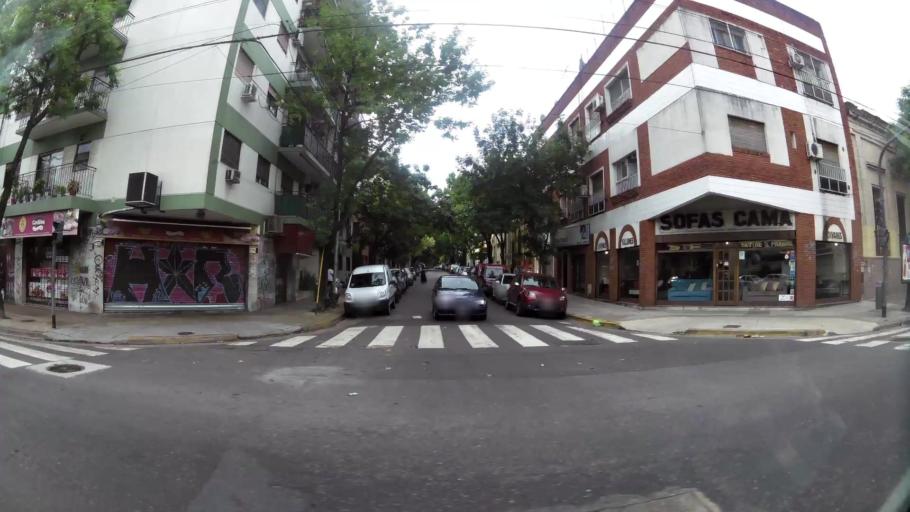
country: AR
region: Buenos Aires F.D.
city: Villa Santa Rita
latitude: -34.6347
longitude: -58.4647
